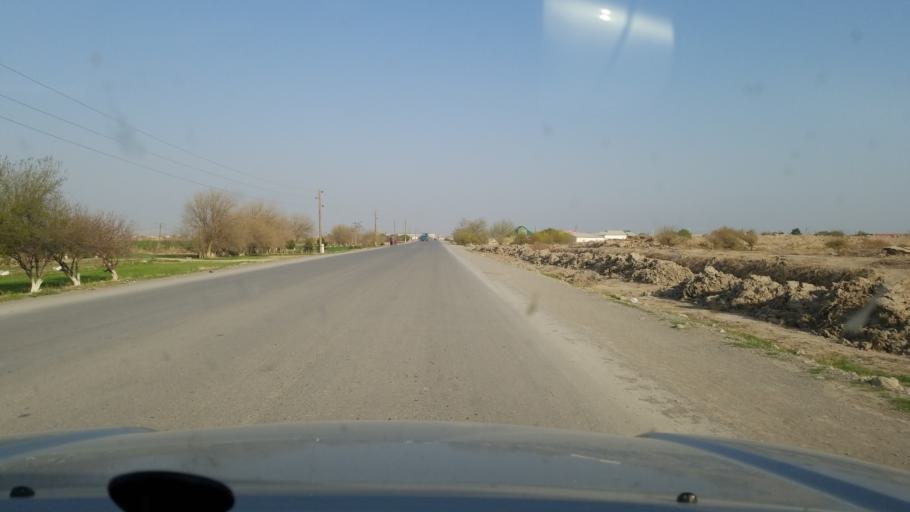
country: AF
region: Jowzjan
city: Qarqin
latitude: 37.5169
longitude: 65.9747
